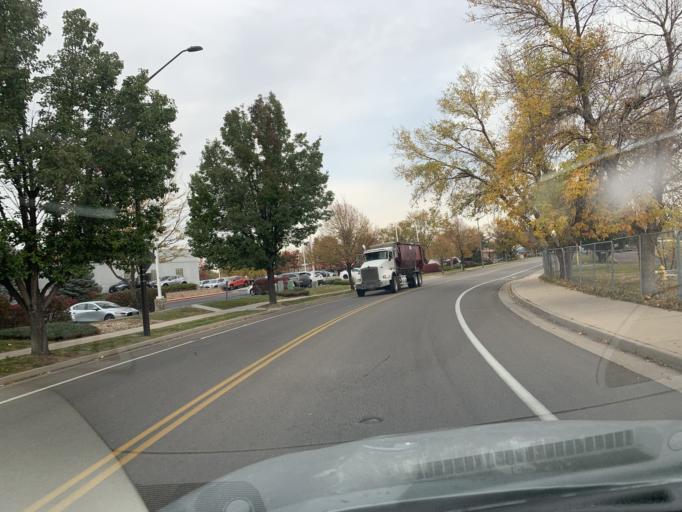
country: US
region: Colorado
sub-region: Larimer County
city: Fort Collins
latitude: 40.5259
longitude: -105.0794
